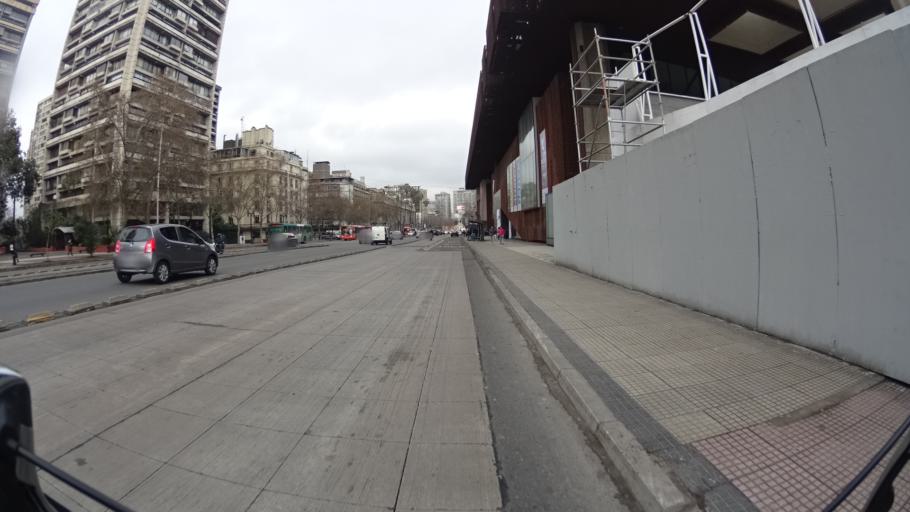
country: CL
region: Santiago Metropolitan
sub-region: Provincia de Santiago
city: Santiago
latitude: -33.4389
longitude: -70.6389
